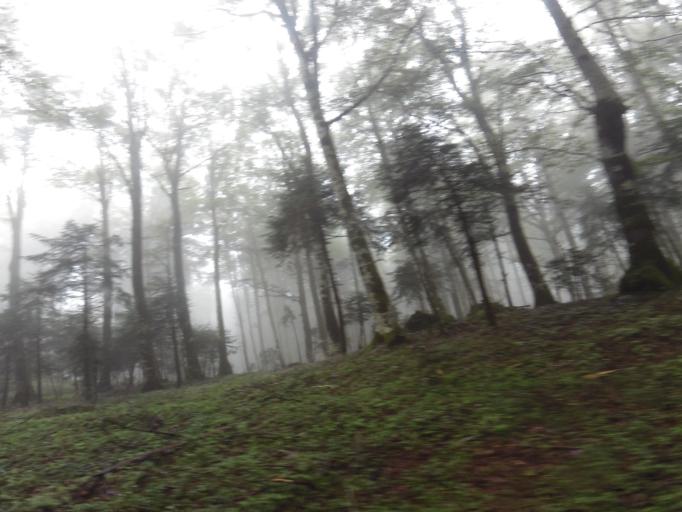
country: IT
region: Calabria
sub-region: Provincia di Vibo-Valentia
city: Mongiana
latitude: 38.5364
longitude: 16.3491
